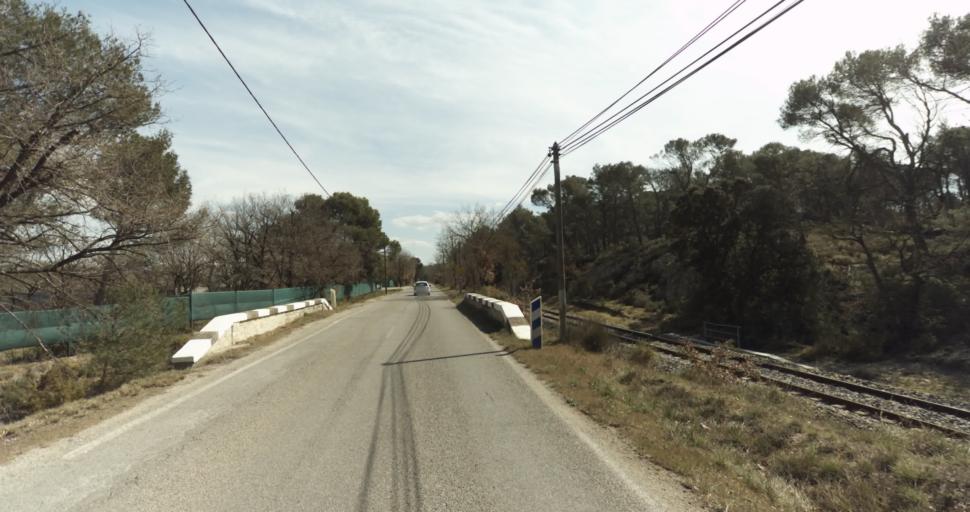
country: FR
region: Provence-Alpes-Cote d'Azur
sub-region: Departement des Bouches-du-Rhone
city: Ventabren
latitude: 43.5071
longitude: 5.3330
